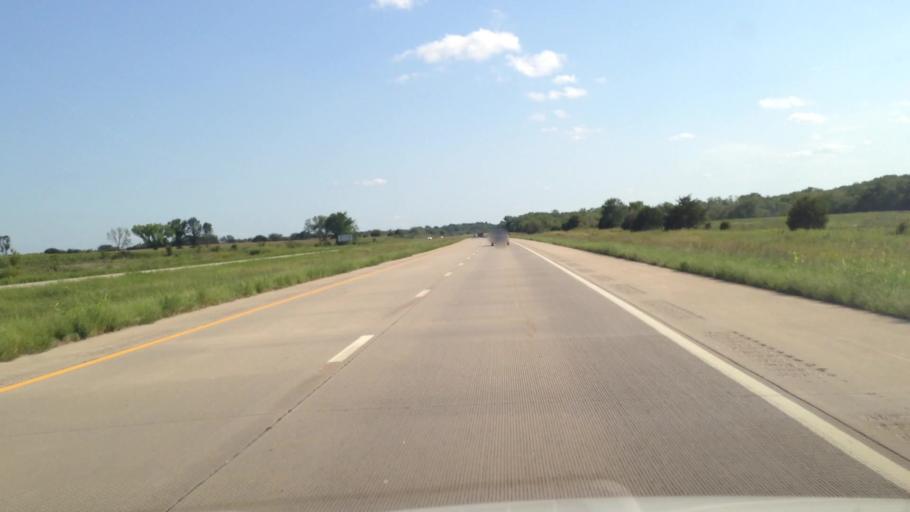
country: US
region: Kansas
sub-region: Bourbon County
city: Fort Scott
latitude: 37.9187
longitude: -94.7045
